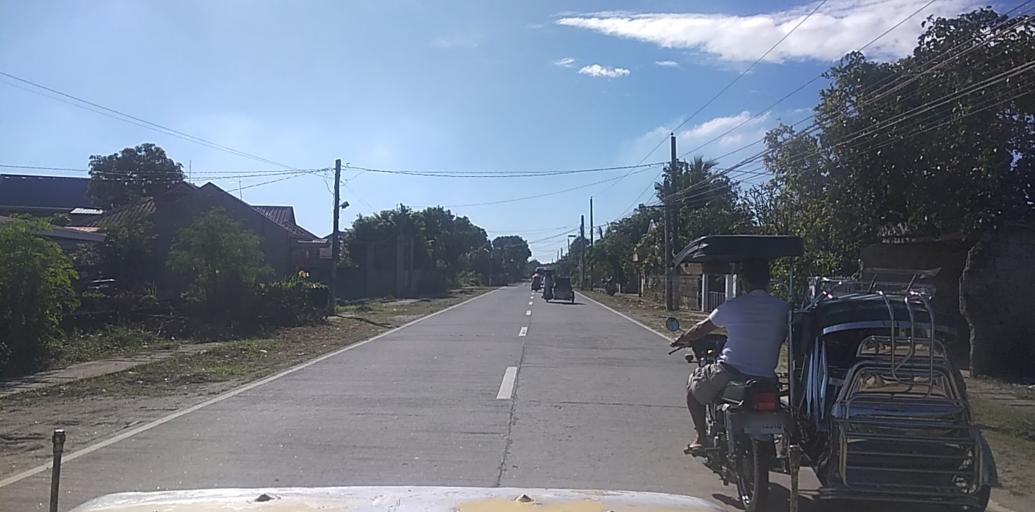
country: PH
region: Central Luzon
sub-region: Province of Pampanga
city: Mexico
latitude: 15.0819
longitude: 120.7166
